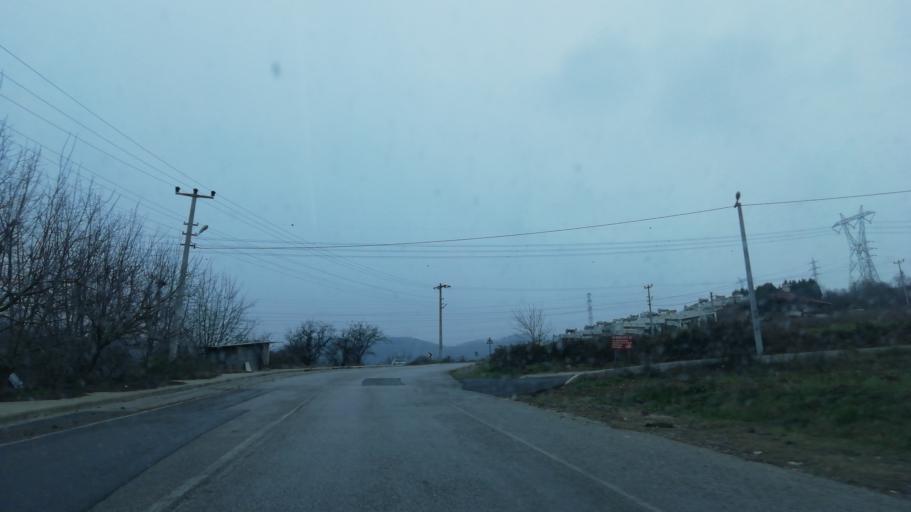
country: TR
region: Sakarya
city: Kazimpasa
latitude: 40.7422
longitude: 30.3090
